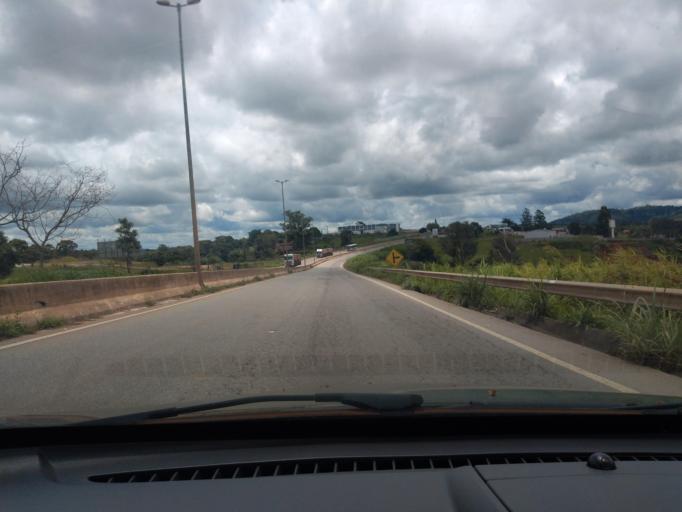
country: BR
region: Minas Gerais
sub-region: Lavras
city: Lavras
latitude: -21.2349
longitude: -45.0330
